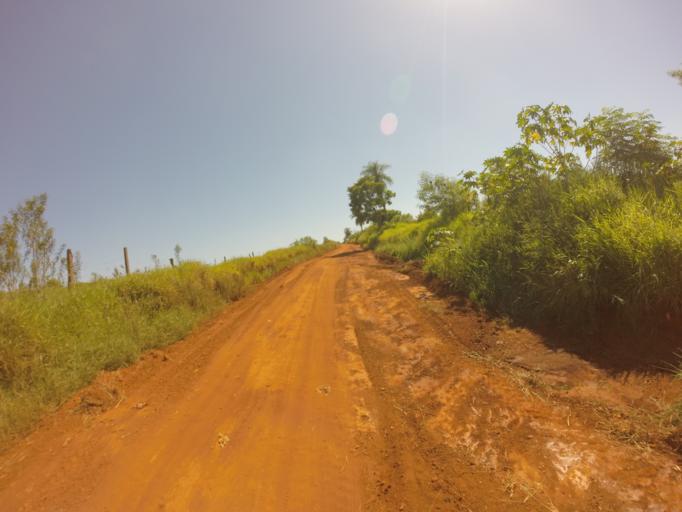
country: PY
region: Alto Parana
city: Ciudad del Este
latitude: -25.4369
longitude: -54.6670
